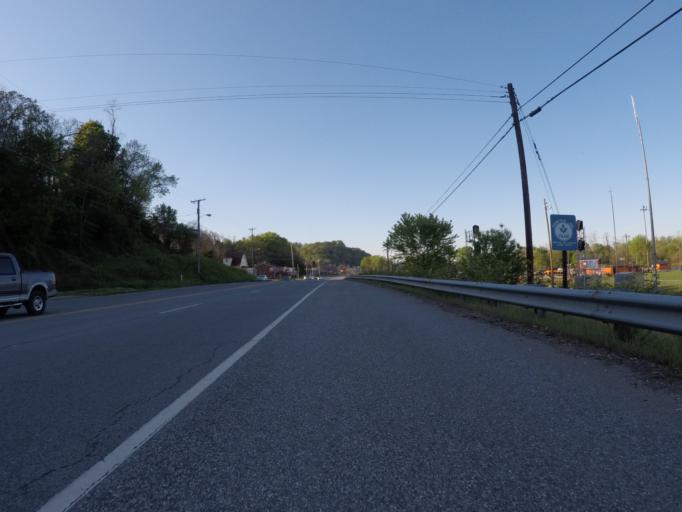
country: US
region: Kentucky
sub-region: Boyd County
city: Catlettsburg
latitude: 38.3987
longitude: -82.6008
